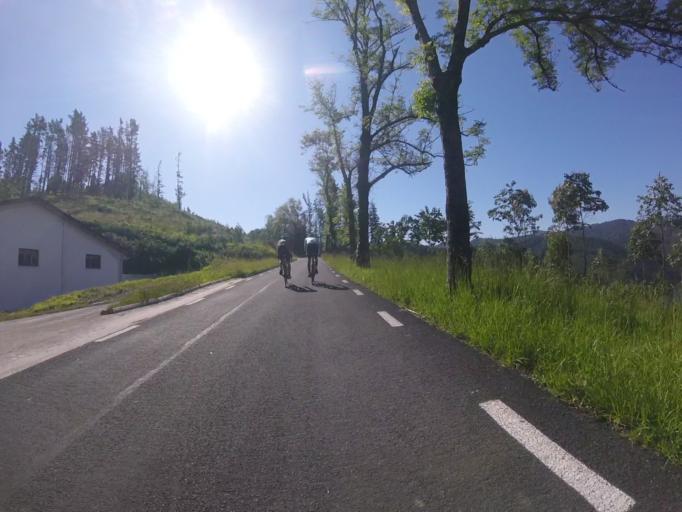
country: ES
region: Basque Country
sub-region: Provincia de Guipuzcoa
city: Beizama
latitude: 43.1343
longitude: -2.2250
